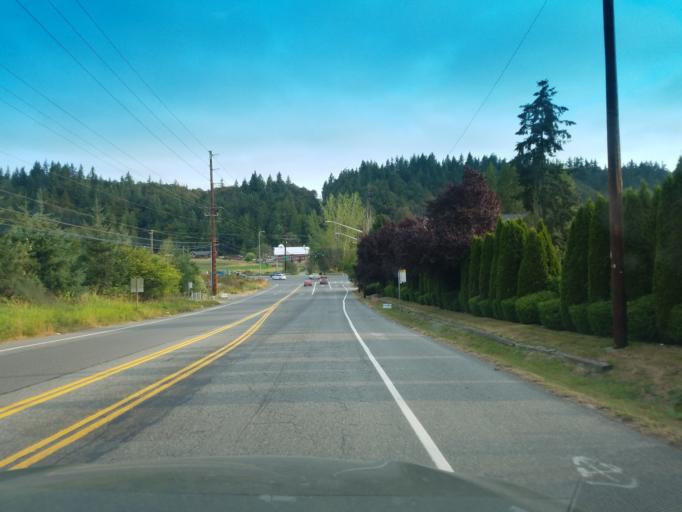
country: US
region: Washington
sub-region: King County
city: Sammamish
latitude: 47.6549
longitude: -122.0627
